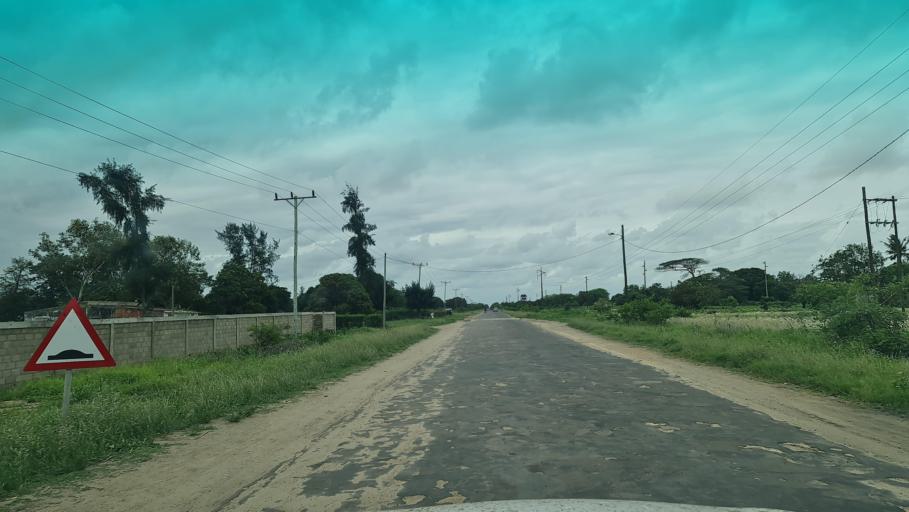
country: MZ
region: Maputo
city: Manhica
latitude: -25.4325
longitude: 32.7731
